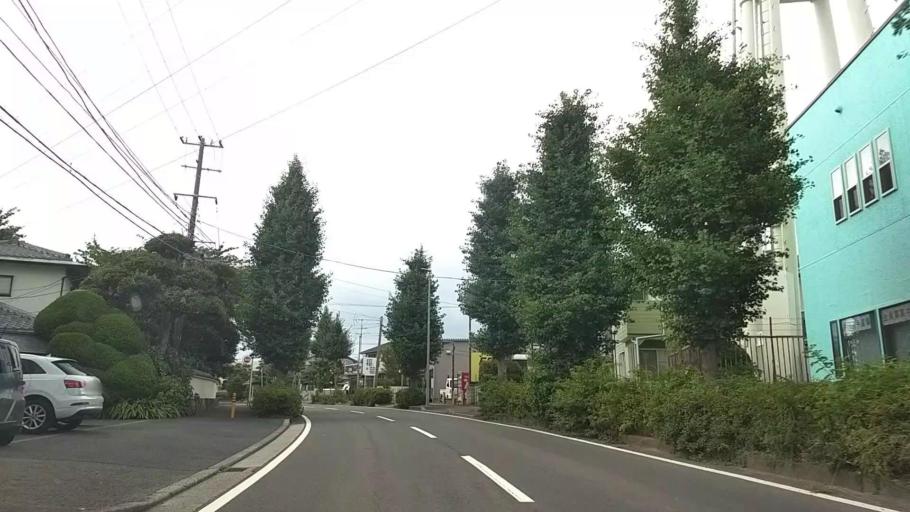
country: JP
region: Kanagawa
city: Fujisawa
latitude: 35.3694
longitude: 139.4313
